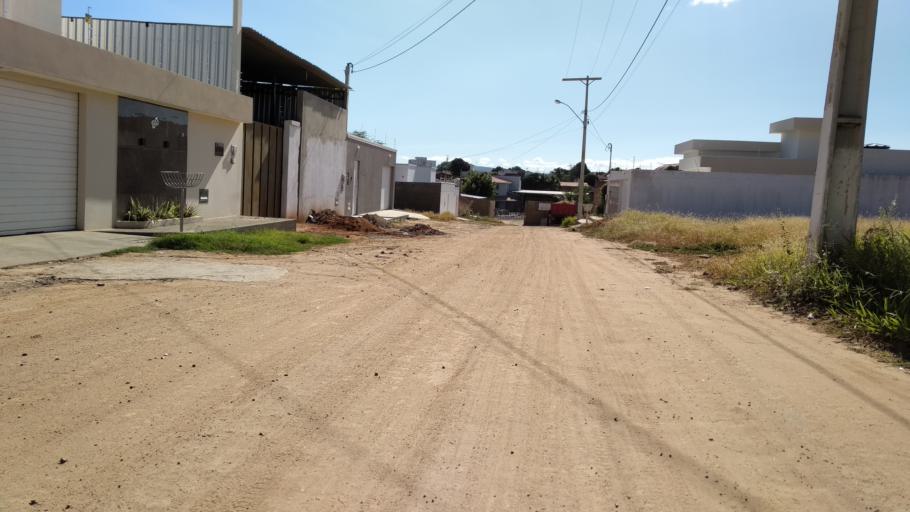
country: BR
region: Bahia
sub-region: Guanambi
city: Guanambi
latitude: -14.2400
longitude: -42.7710
